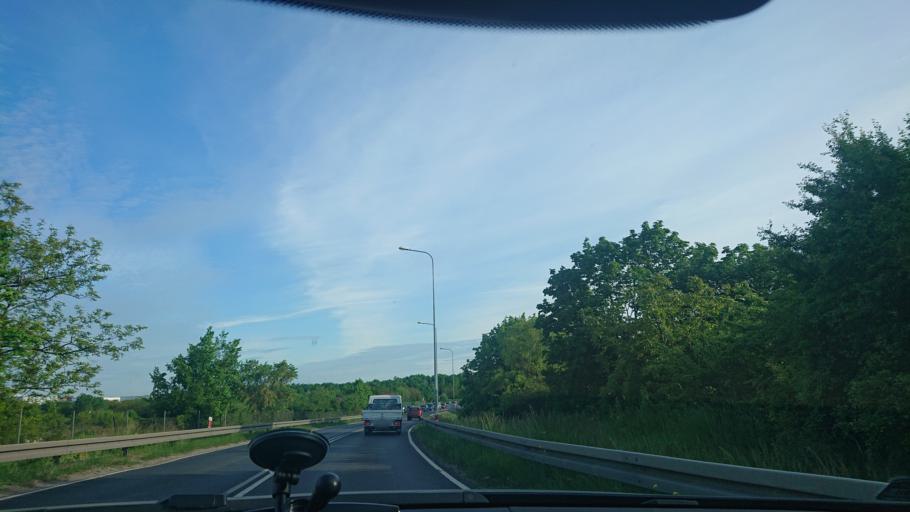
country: PL
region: Greater Poland Voivodeship
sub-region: Powiat gnieznienski
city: Gniezno
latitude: 52.5257
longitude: 17.5856
